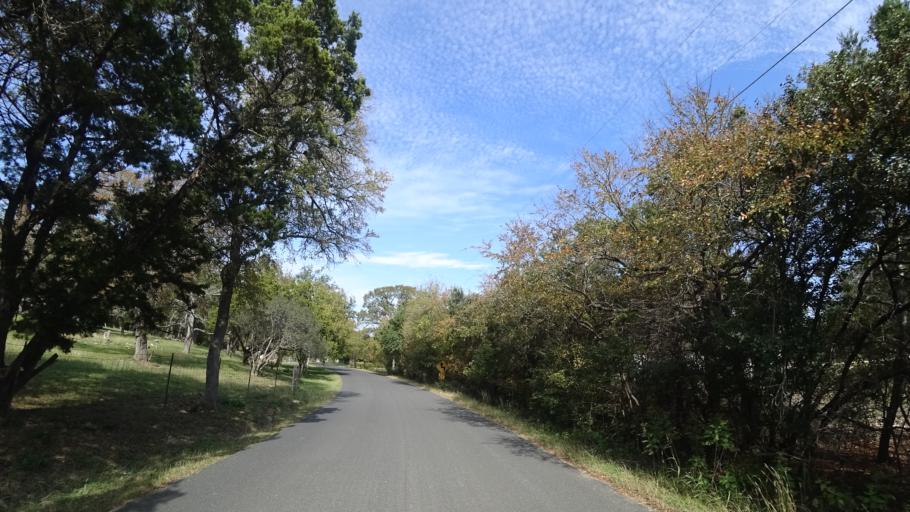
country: US
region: Texas
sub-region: Travis County
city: Barton Creek
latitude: 30.2221
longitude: -97.9291
